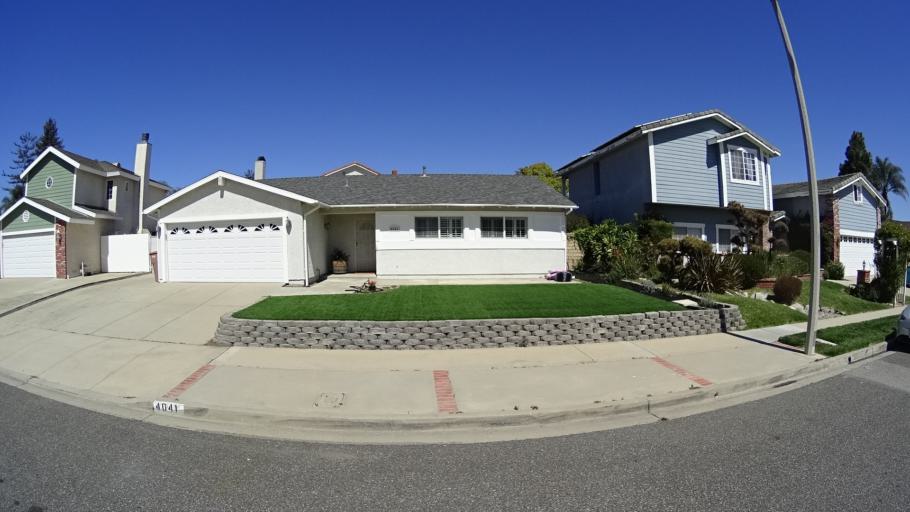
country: US
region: California
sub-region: Ventura County
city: Casa Conejo
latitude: 34.1583
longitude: -118.9611
